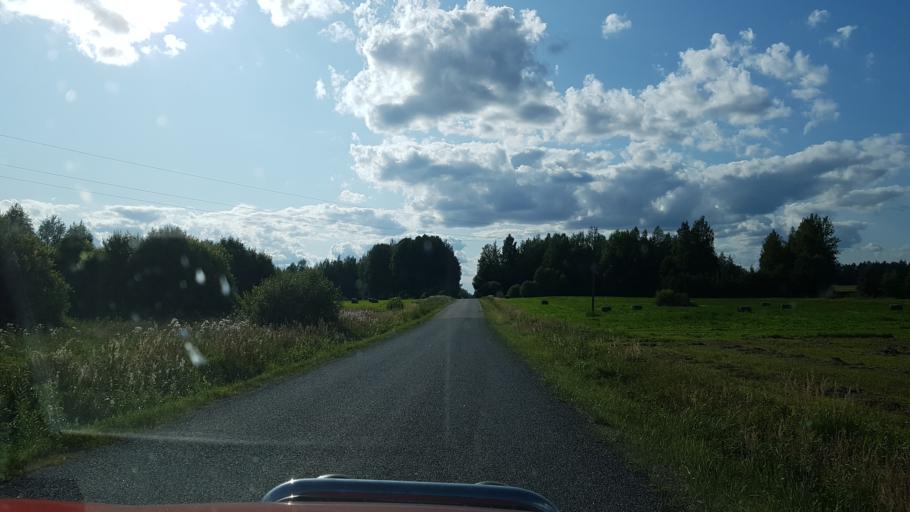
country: EE
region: Vorumaa
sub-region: Voru linn
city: Voru
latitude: 57.9266
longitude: 27.0869
